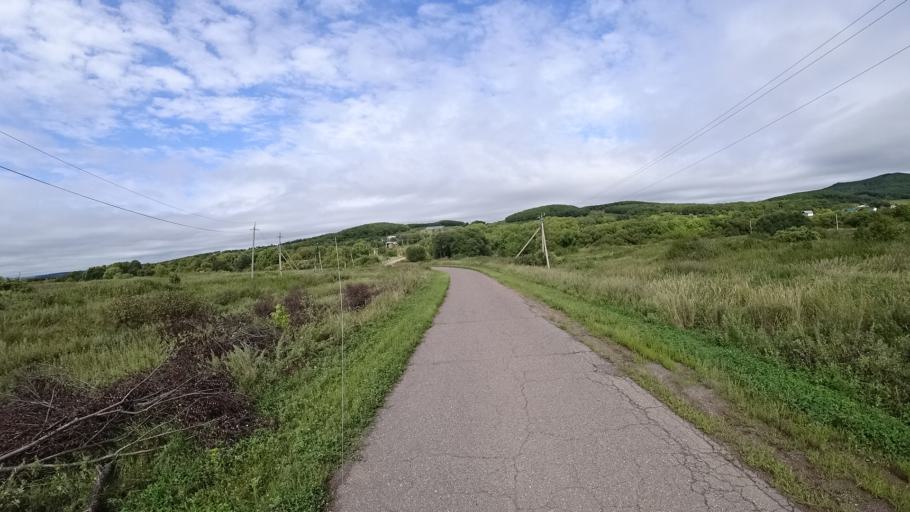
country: RU
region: Primorskiy
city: Lyalichi
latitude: 44.1342
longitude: 132.3879
